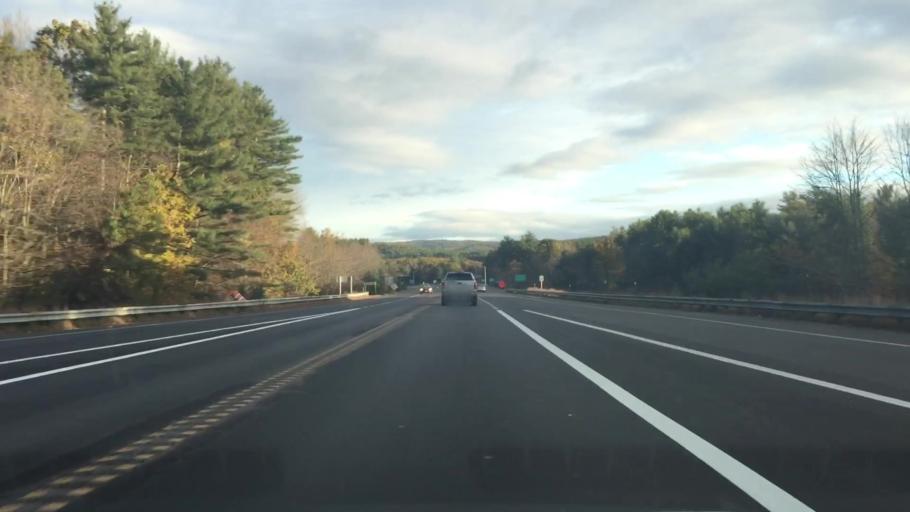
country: US
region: New Hampshire
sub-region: Cheshire County
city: Keene
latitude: 42.9369
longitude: -72.2966
